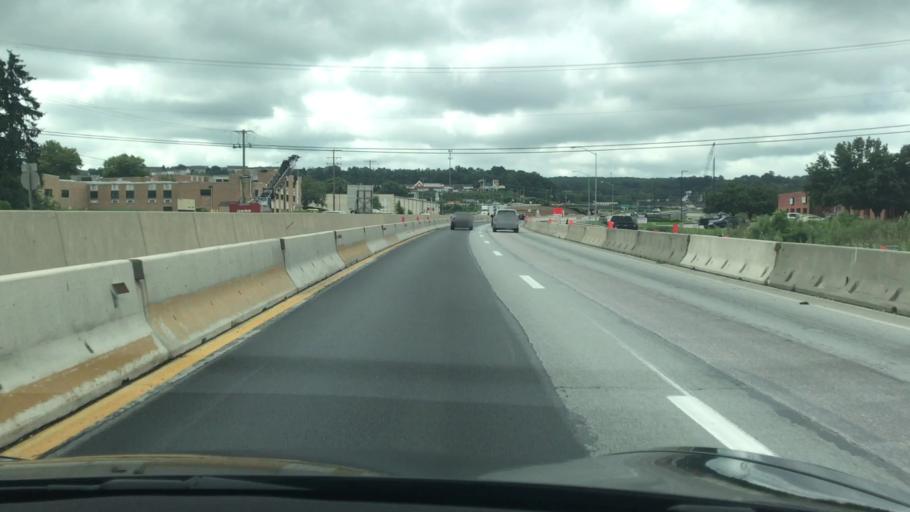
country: US
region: Pennsylvania
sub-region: York County
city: East York
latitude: 39.9627
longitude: -76.6858
